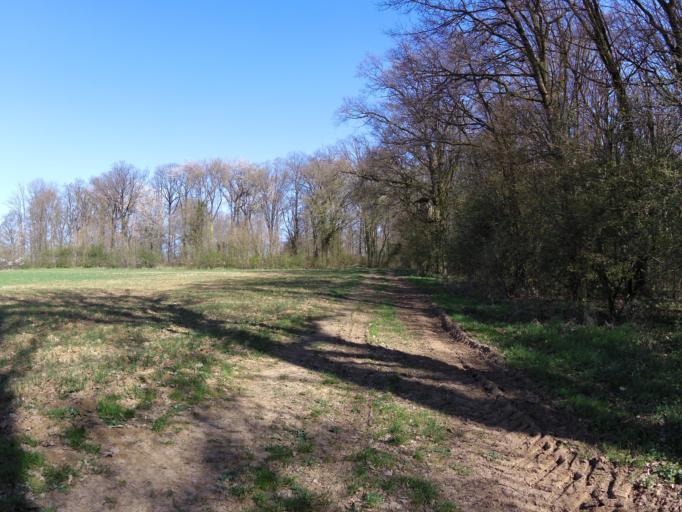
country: DE
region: Bavaria
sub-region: Regierungsbezirk Unterfranken
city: Kurnach
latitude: 49.8324
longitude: 10.0529
